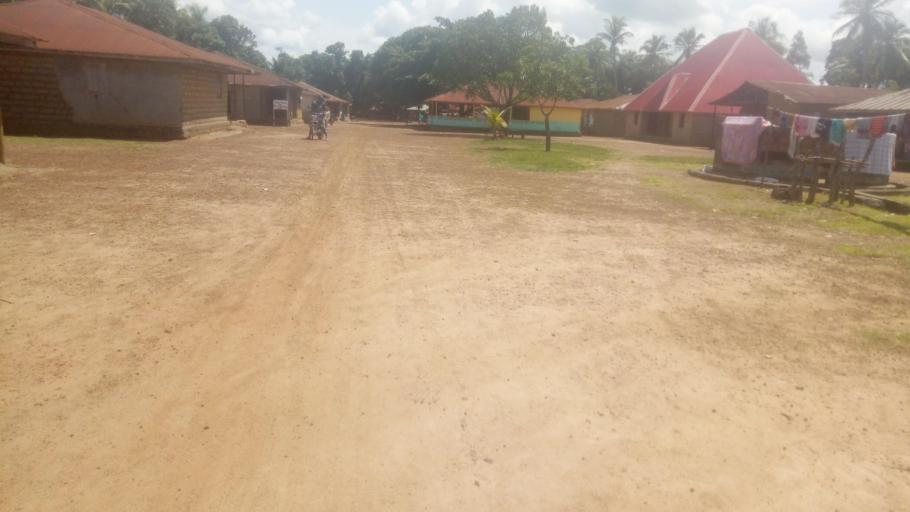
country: SL
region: Northern Province
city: Magburaka
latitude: 8.6401
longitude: -12.0593
